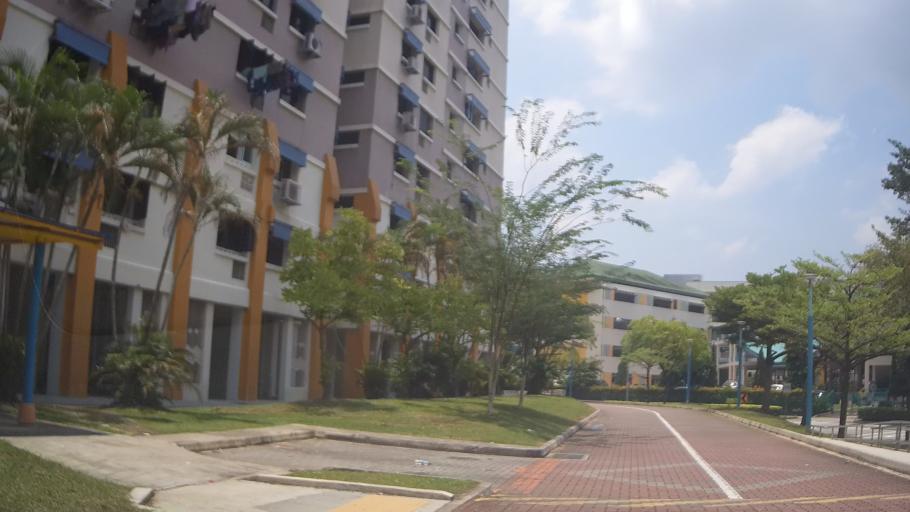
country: MY
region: Johor
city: Johor Bahru
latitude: 1.4447
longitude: 103.7959
